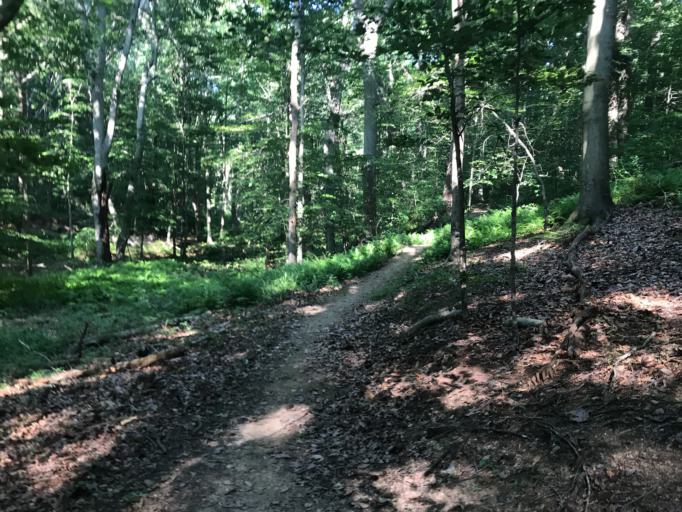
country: US
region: Delaware
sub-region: New Castle County
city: Newark
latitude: 39.7233
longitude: -75.7840
